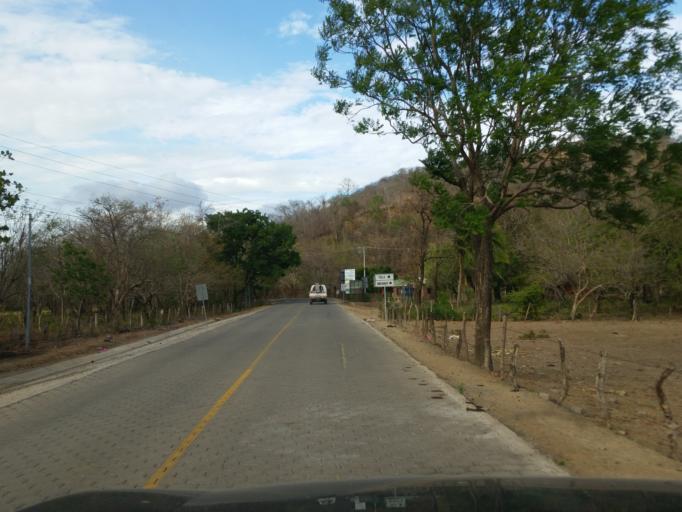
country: NI
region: Rivas
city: Tola
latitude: 11.3925
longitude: -85.9614
